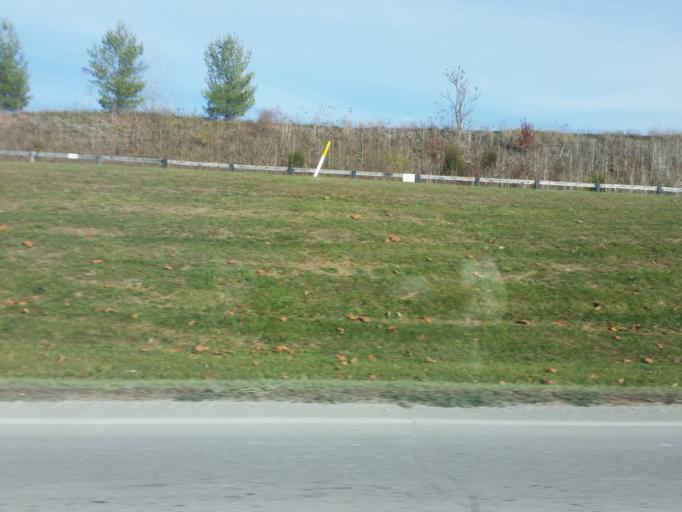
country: US
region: Kentucky
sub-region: Pendleton County
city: Falmouth
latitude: 38.7951
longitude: -84.3540
